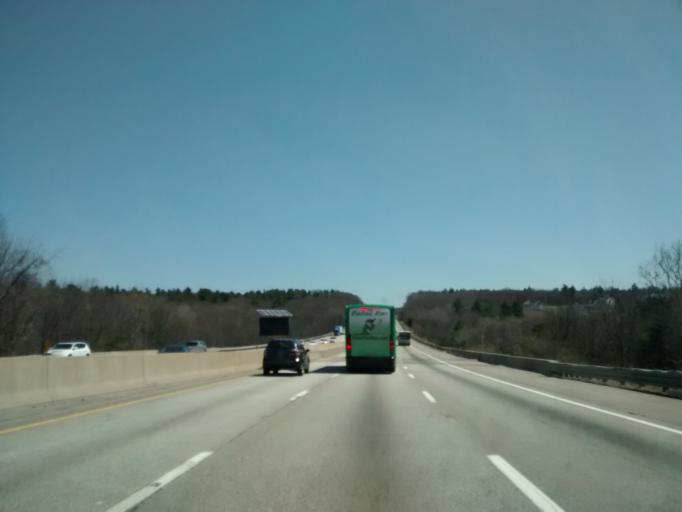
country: US
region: Massachusetts
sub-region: Worcester County
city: Grafton
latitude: 42.2287
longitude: -71.6538
